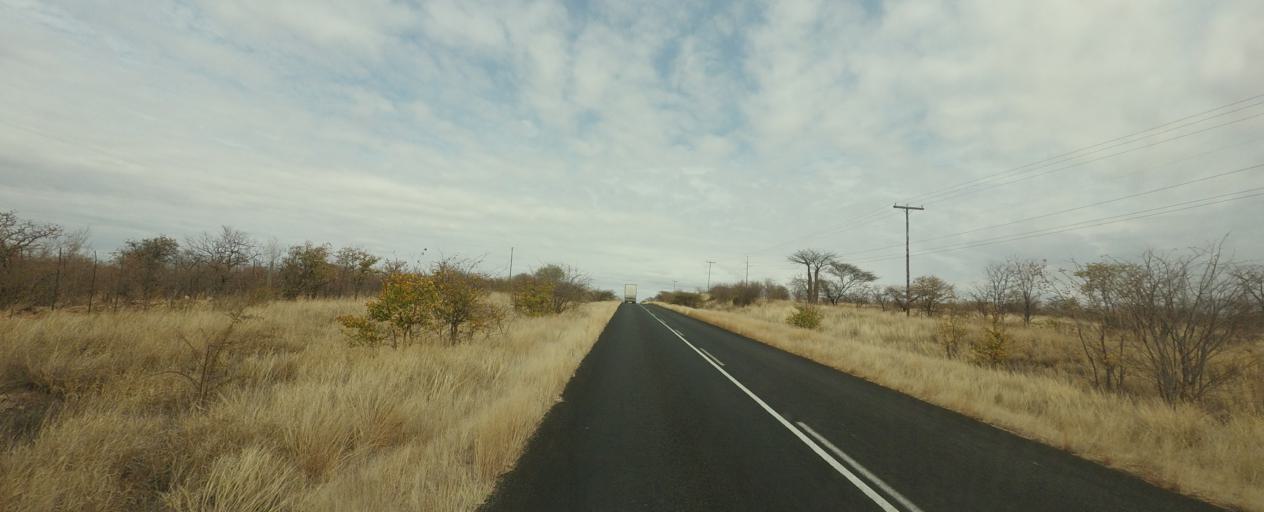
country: ZW
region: Matabeleland South
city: Beitbridge
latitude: -22.4297
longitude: 29.4277
